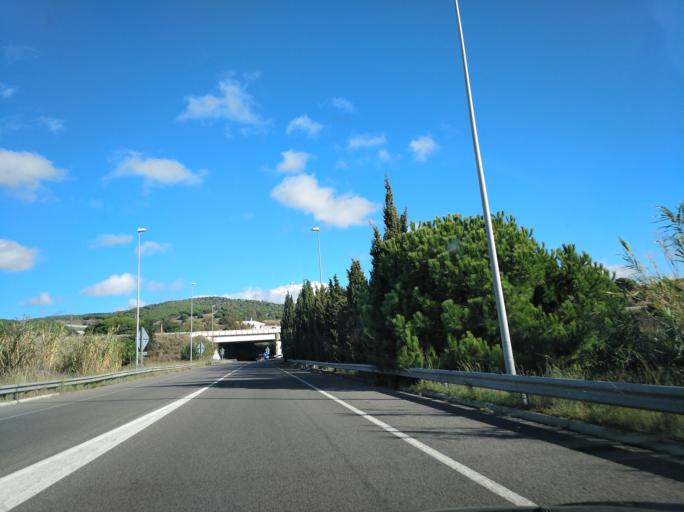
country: ES
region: Catalonia
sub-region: Provincia de Barcelona
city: Mataro
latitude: 41.5557
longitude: 2.4577
